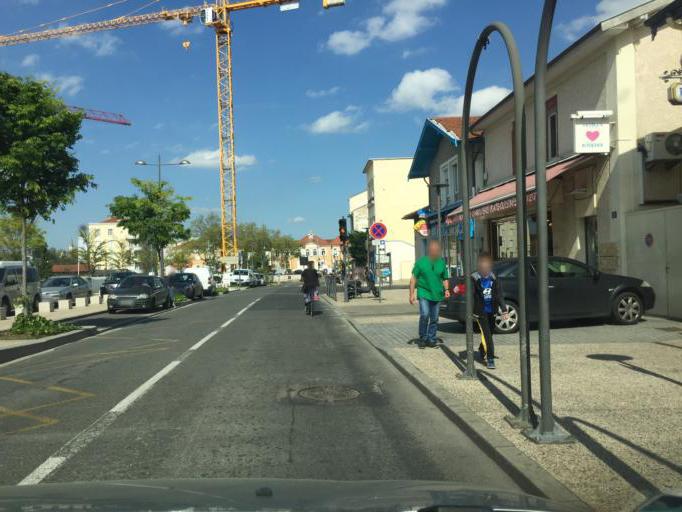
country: FR
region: Rhone-Alpes
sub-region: Departement du Rhone
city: Sathonay-Camp
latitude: 45.8235
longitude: 4.8738
